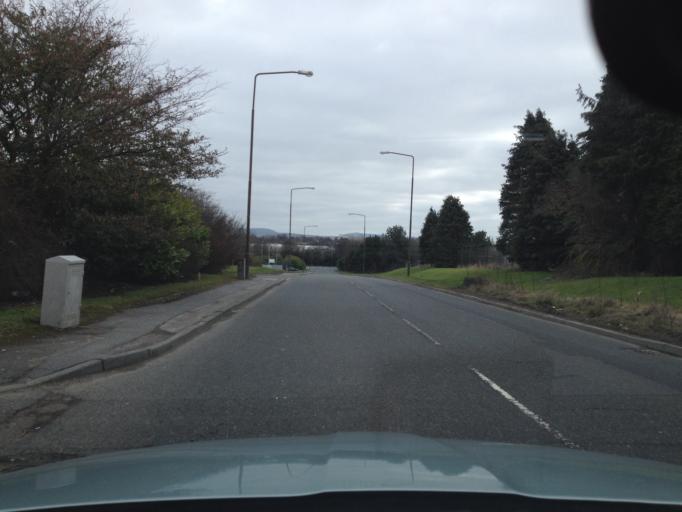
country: GB
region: Scotland
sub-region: West Lothian
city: Livingston
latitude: 55.9113
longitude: -3.5069
